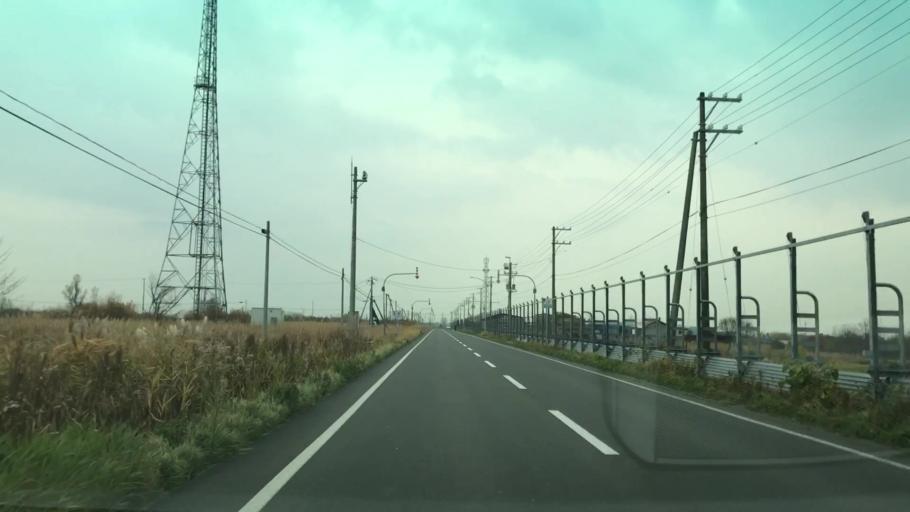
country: JP
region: Hokkaido
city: Ishikari
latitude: 43.2925
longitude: 141.4105
